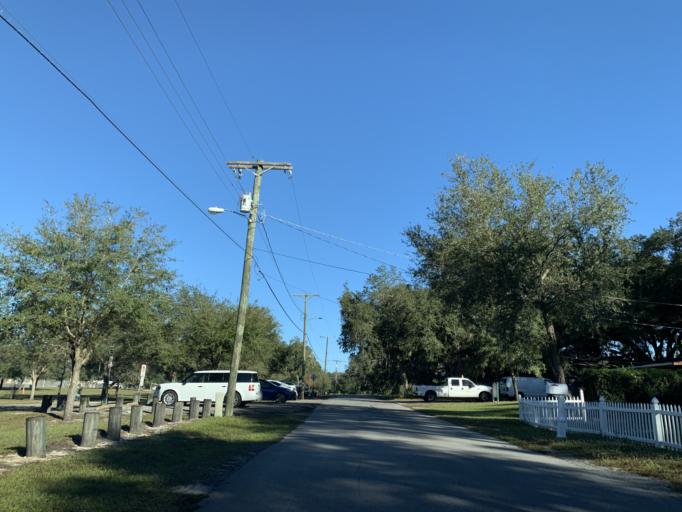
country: US
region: Florida
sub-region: Hillsborough County
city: Temple Terrace
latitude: 28.0268
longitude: -82.4287
